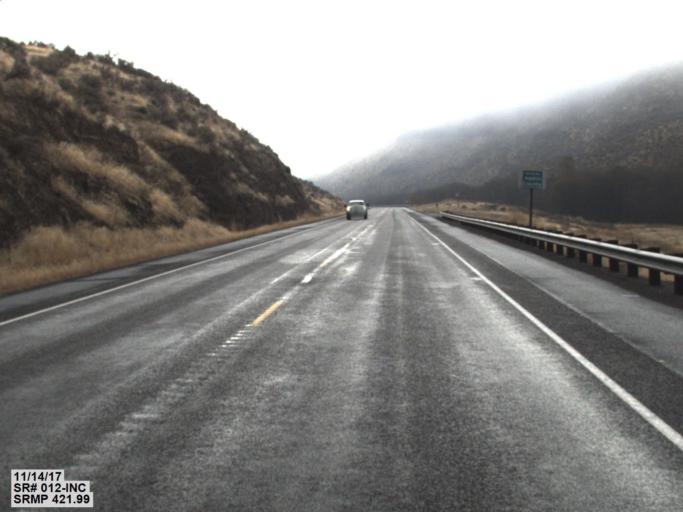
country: US
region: Washington
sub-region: Asotin County
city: Clarkston Heights-Vineland
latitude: 46.4116
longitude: -117.2690
